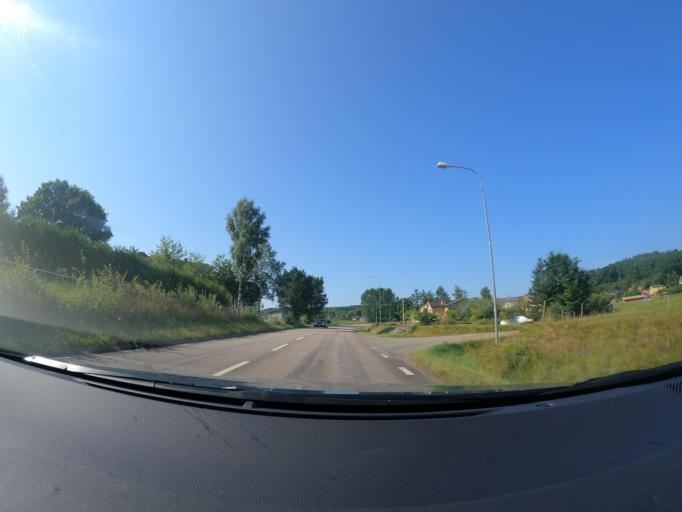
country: SE
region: Halland
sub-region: Falkenbergs Kommun
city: Falkenberg
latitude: 57.0651
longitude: 12.6497
